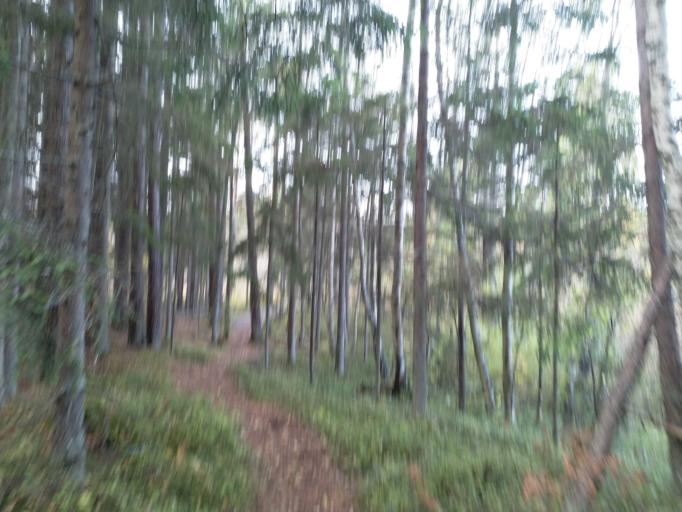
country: LV
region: Dundaga
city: Dundaga
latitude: 57.6485
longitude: 22.2581
